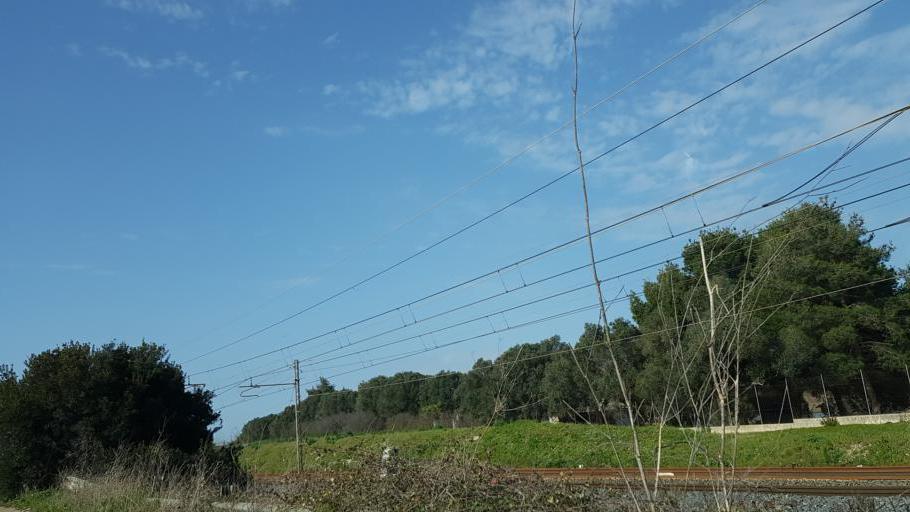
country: IT
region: Apulia
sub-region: Provincia di Brindisi
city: Brindisi
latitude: 40.6233
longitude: 17.9043
